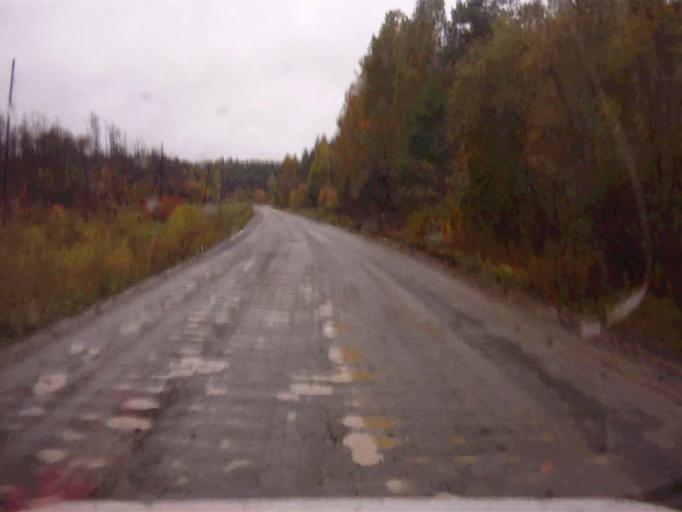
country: RU
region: Chelyabinsk
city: Kyshtym
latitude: 55.7425
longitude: 60.5037
